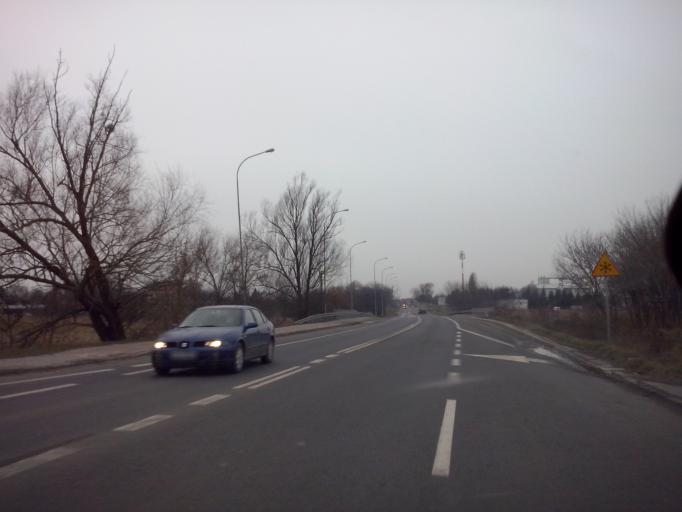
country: PL
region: Lublin Voivodeship
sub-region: Zamosc
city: Zamosc
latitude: 50.7370
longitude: 23.2448
